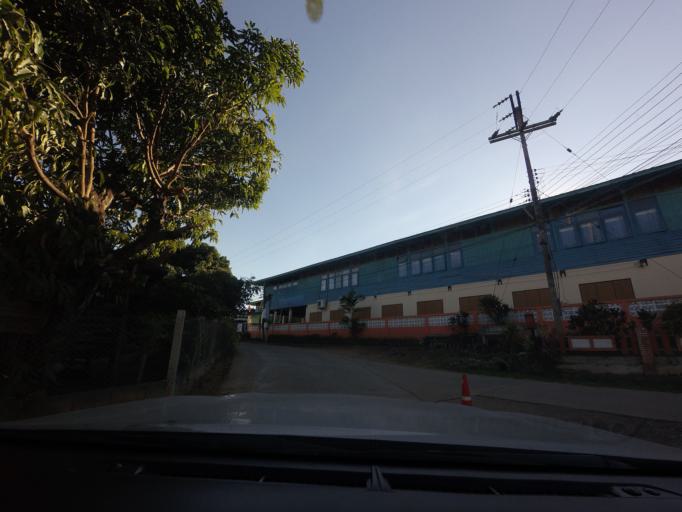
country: TH
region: Mae Hong Son
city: Wiang Nuea
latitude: 19.3942
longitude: 98.4215
